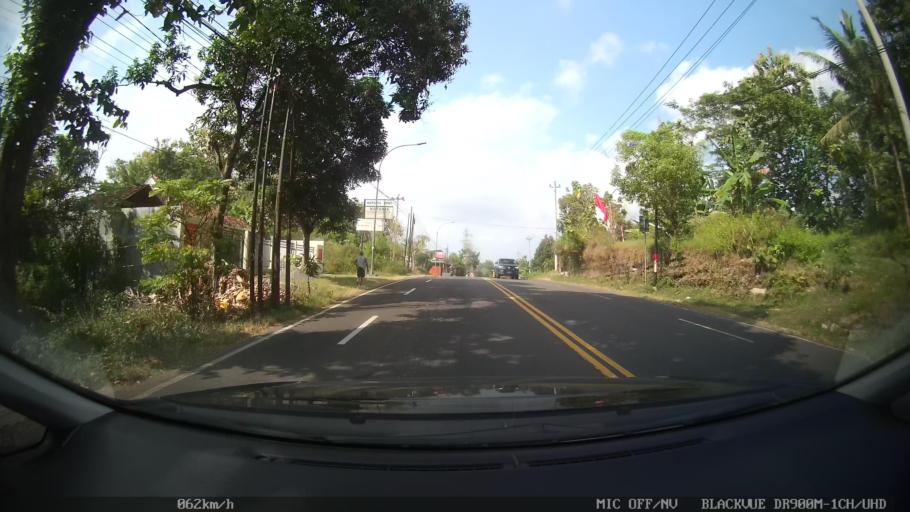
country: ID
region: Daerah Istimewa Yogyakarta
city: Srandakan
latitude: -7.8612
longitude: 110.2115
